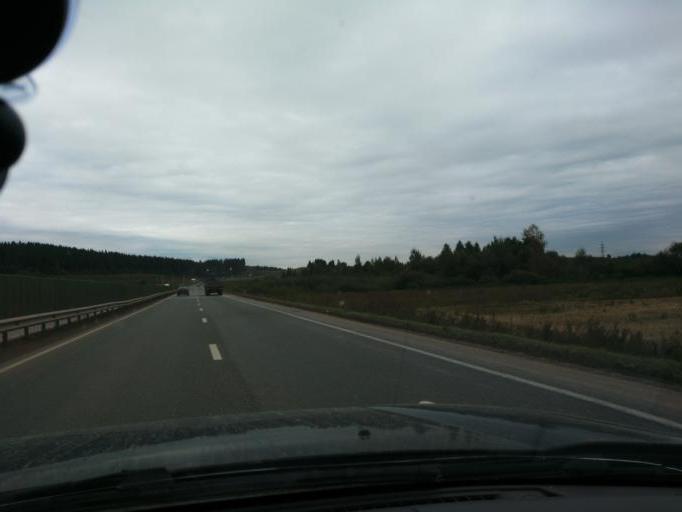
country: RU
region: Perm
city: Froly
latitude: 57.9324
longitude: 56.2045
